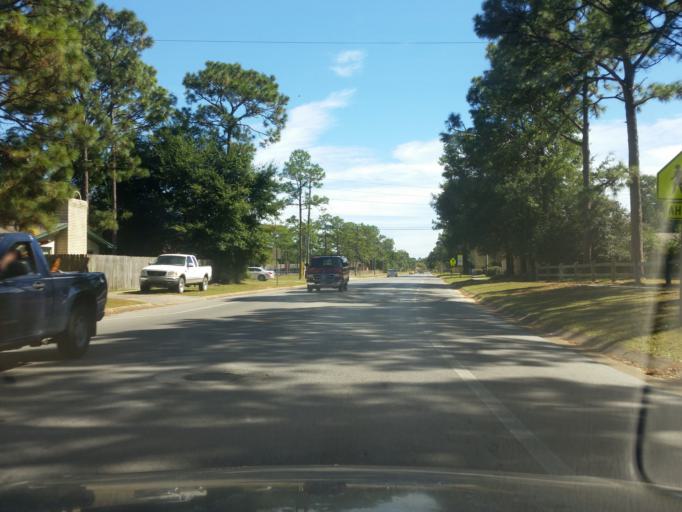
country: US
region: Florida
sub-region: Escambia County
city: Ferry Pass
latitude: 30.4881
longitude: -87.1803
